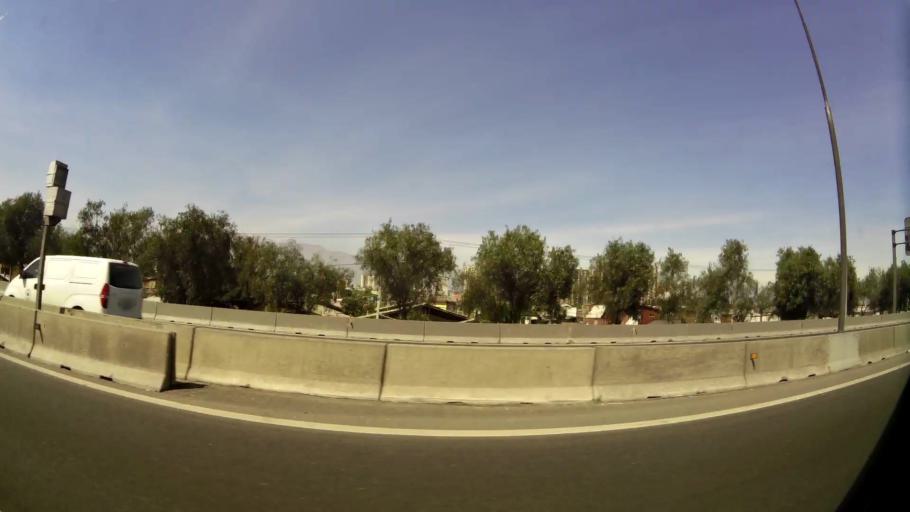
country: CL
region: Santiago Metropolitan
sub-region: Provincia de Santiago
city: Santiago
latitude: -33.5098
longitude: -70.6706
